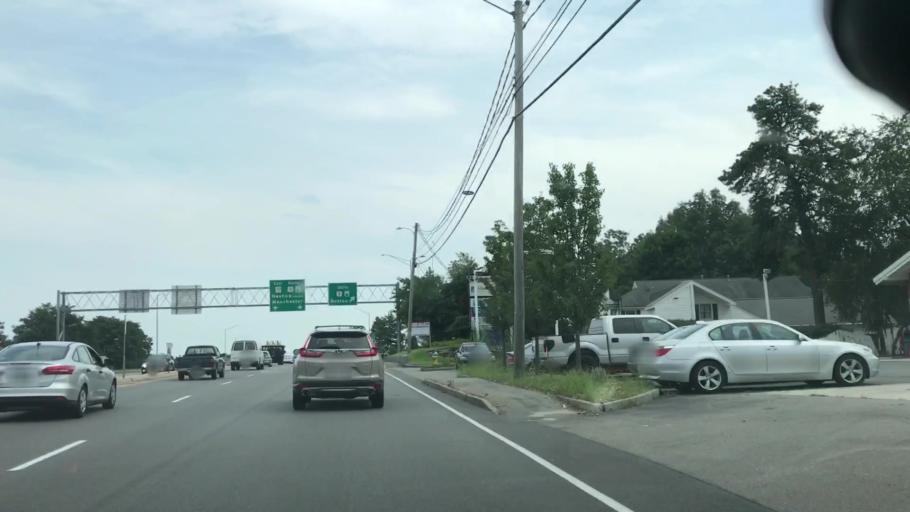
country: US
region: New Hampshire
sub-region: Hillsborough County
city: Nashua
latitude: 42.7778
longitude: -71.4958
